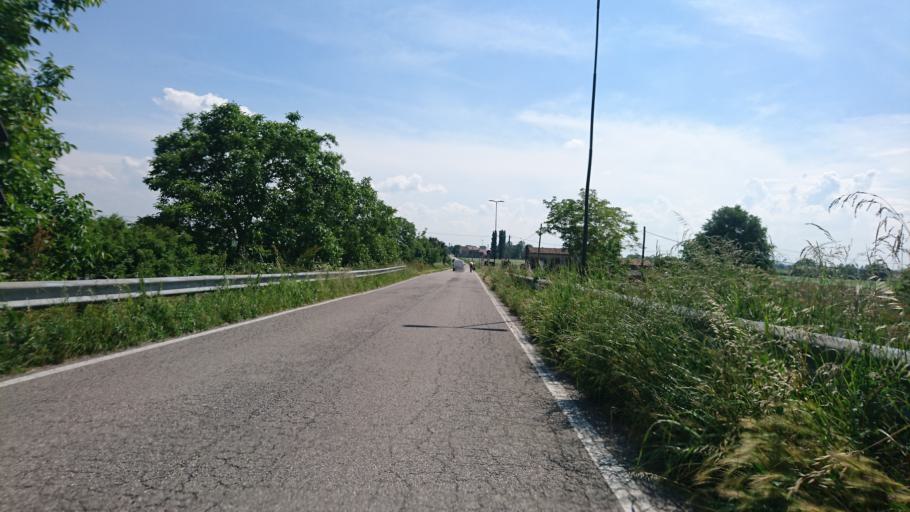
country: IT
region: Veneto
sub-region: Provincia di Rovigo
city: Castelmassa
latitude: 45.0733
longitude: 11.3383
